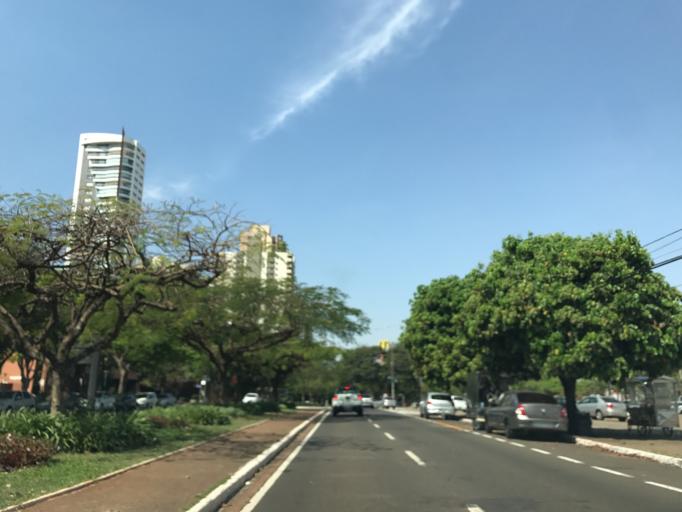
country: BR
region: Parana
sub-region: Maringa
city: Maringa
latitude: -23.4257
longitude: -51.9383
